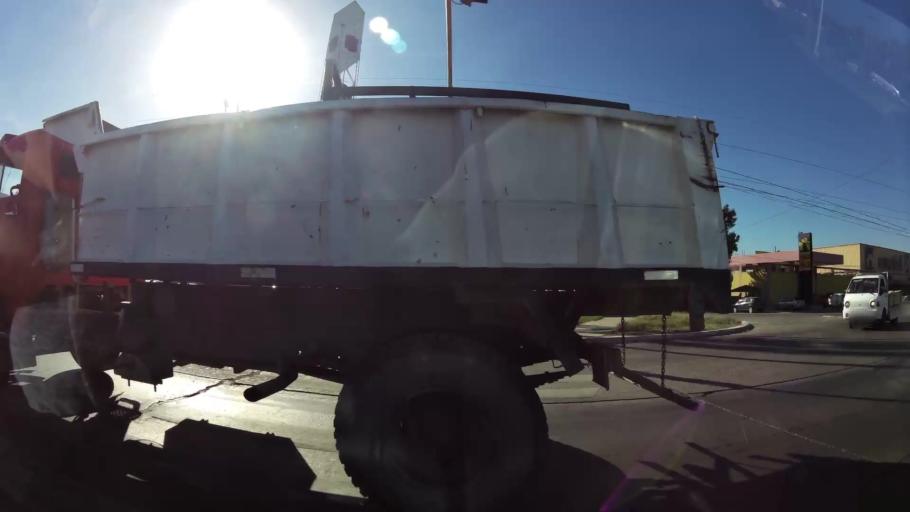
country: AR
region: Mendoza
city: Las Heras
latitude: -32.8553
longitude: -68.8065
